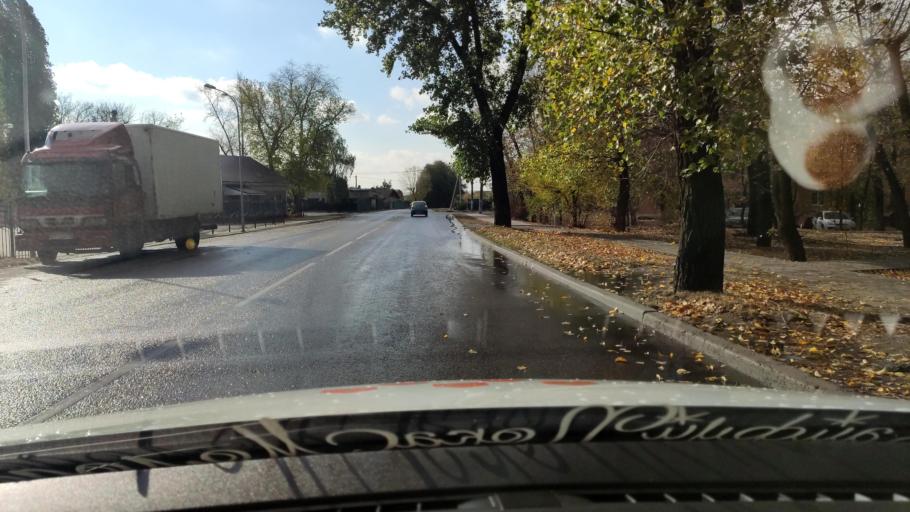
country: RU
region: Voronezj
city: Pridonskoy
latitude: 51.6835
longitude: 39.0769
